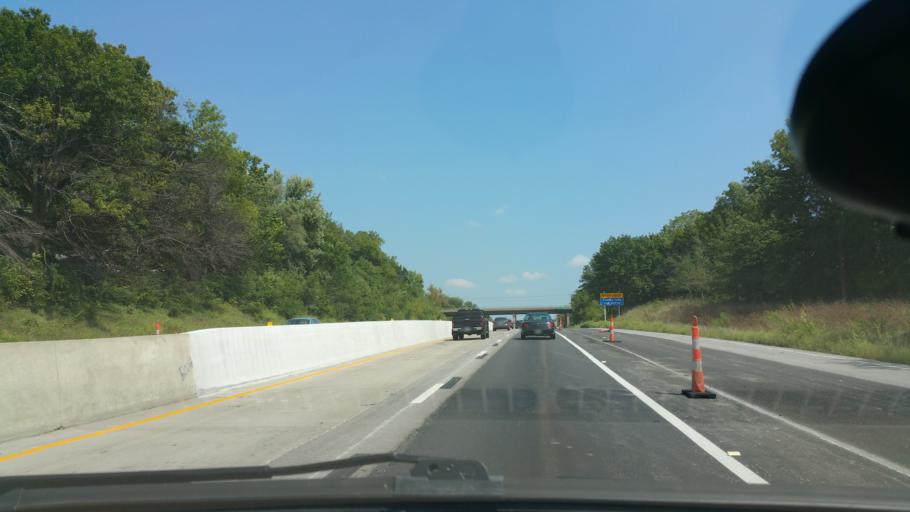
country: US
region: Missouri
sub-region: Clay County
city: Claycomo
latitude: 39.2028
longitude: -94.5030
